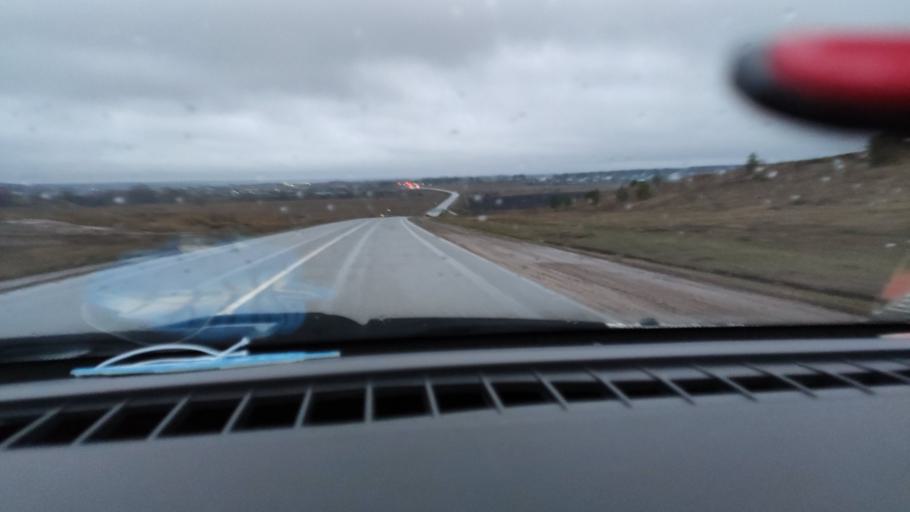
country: RU
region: Udmurtiya
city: Alnashi
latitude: 56.1910
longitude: 52.4564
